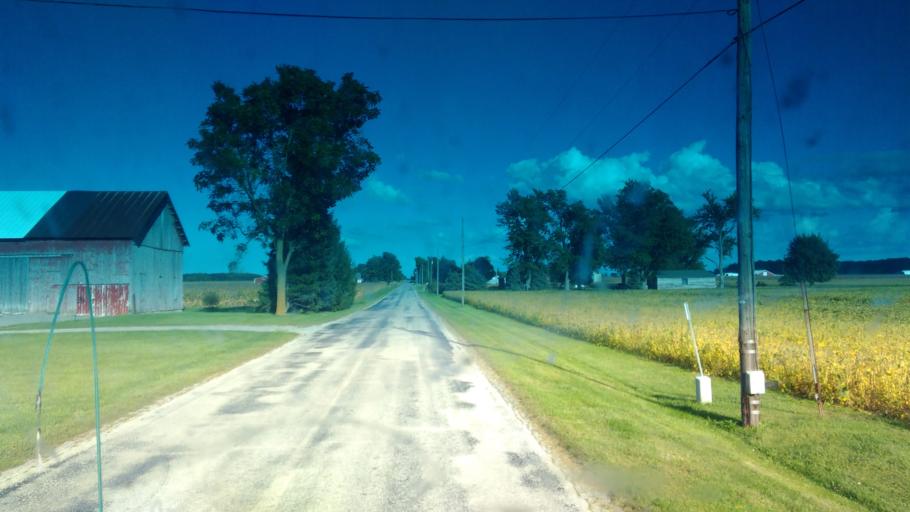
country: US
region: Ohio
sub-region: Hancock County
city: Arlington
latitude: 40.9356
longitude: -83.6398
